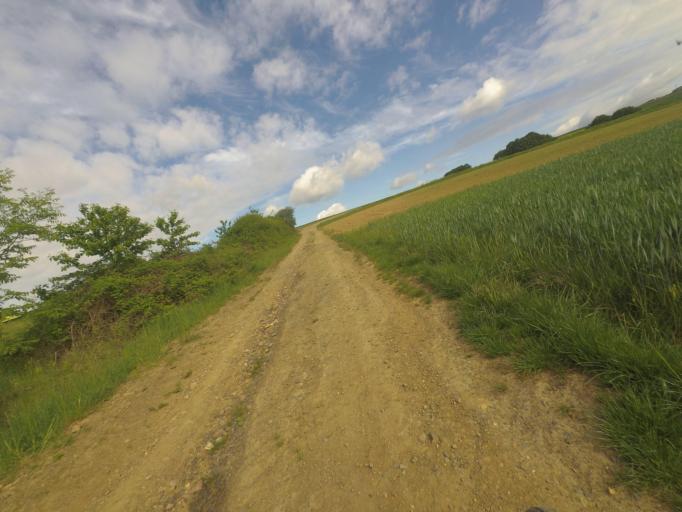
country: DE
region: Rheinland-Pfalz
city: Orbis
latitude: 49.6820
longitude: 8.0044
